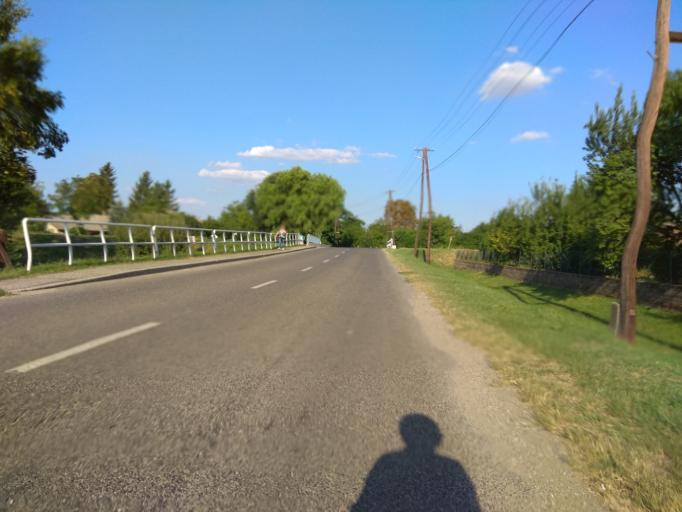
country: HU
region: Borsod-Abauj-Zemplen
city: Nyekladhaza
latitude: 47.9598
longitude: 20.8810
